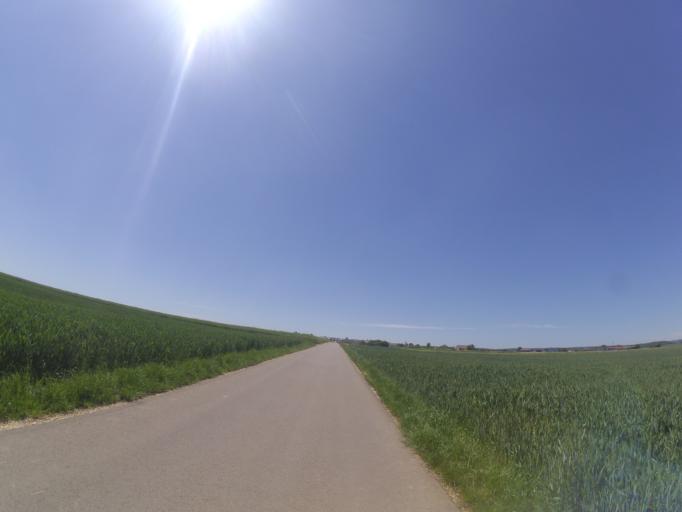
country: DE
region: Baden-Wuerttemberg
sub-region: Tuebingen Region
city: Blaubeuren
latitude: 48.4710
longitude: 9.8503
